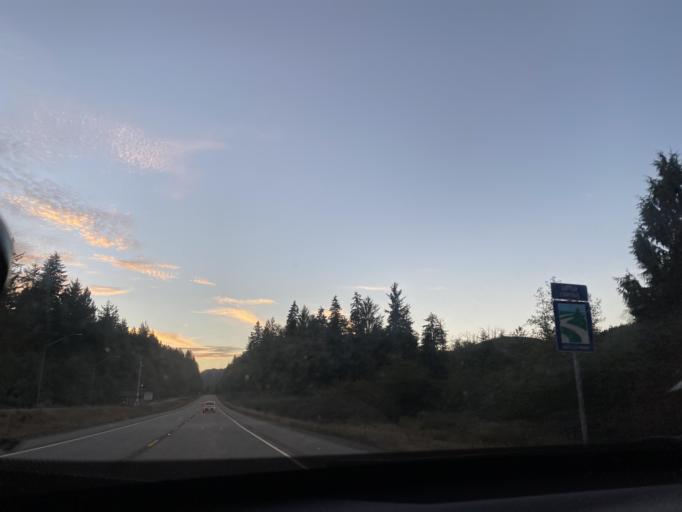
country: US
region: Washington
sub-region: Clallam County
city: Port Angeles
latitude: 48.0689
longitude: -123.6242
